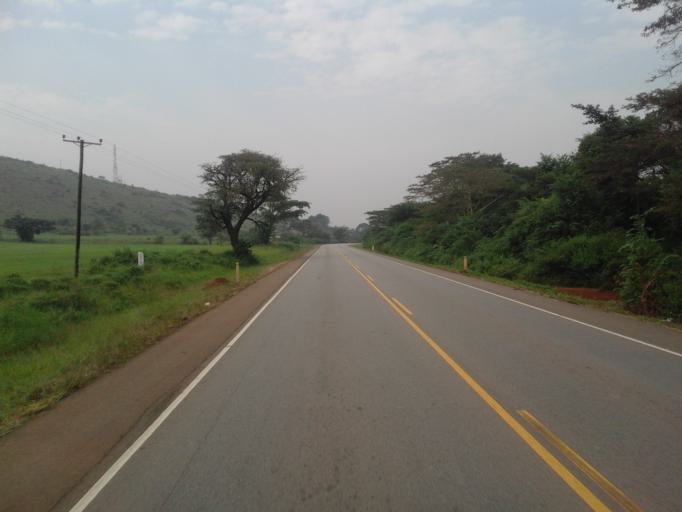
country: UG
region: Eastern Region
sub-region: Busia District
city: Busia
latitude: 0.5473
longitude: 34.0177
